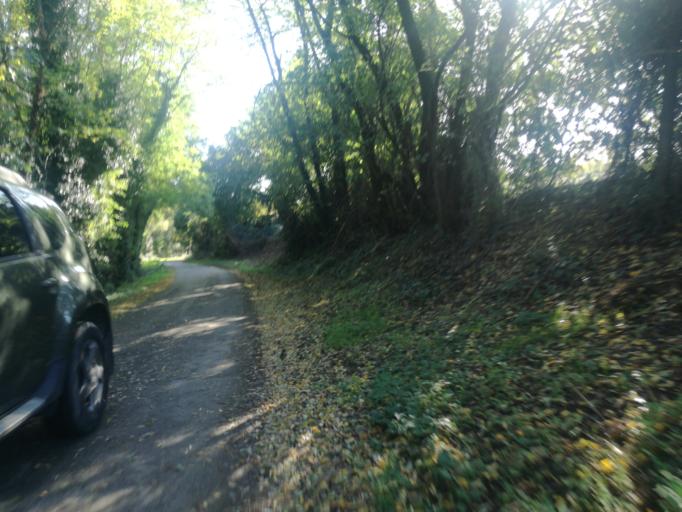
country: IT
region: Lombardy
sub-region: Provincia di Bergamo
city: Bottanuco
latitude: 45.6264
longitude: 9.5017
